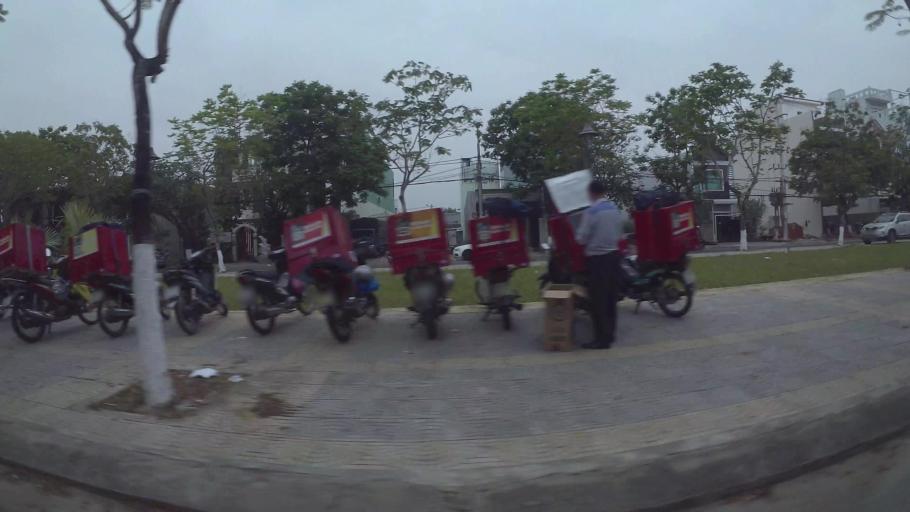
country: VN
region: Da Nang
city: Thanh Khe
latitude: 16.0499
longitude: 108.1787
